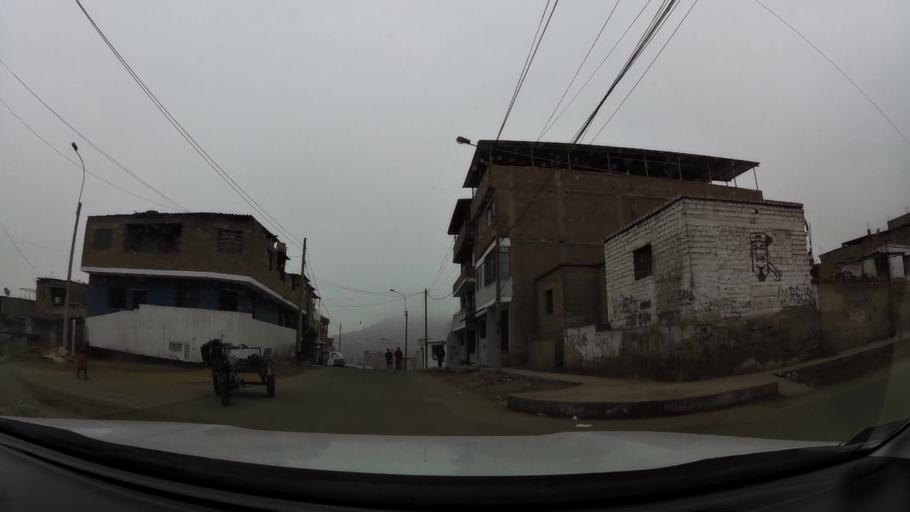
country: PE
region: Lima
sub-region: Lima
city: Surco
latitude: -12.1612
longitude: -76.9507
